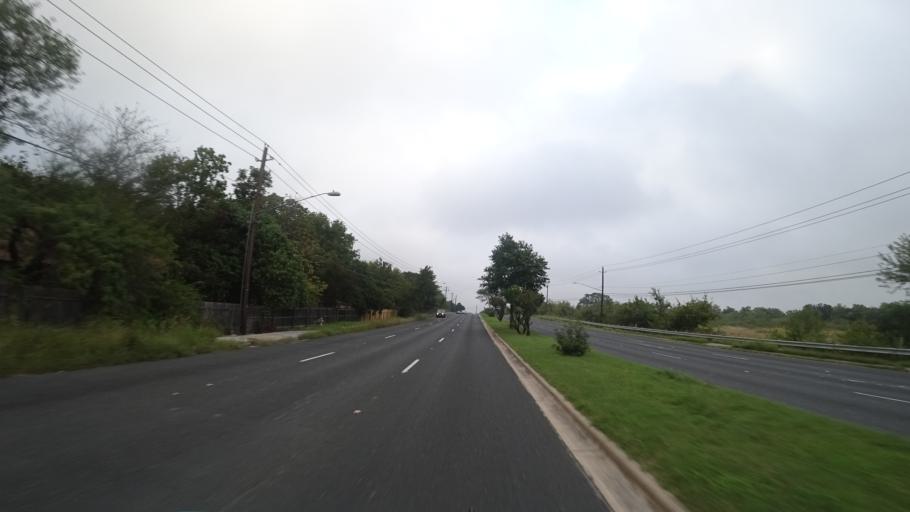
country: US
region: Texas
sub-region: Travis County
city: Wells Branch
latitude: 30.3601
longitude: -97.6701
